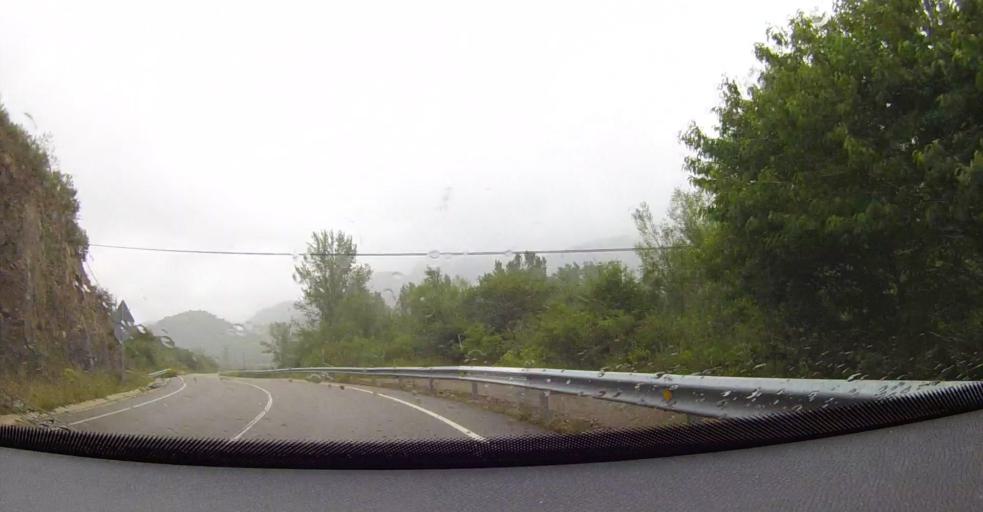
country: ES
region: Castille and Leon
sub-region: Provincia de Leon
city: Acebedo
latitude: 43.0422
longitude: -5.1107
